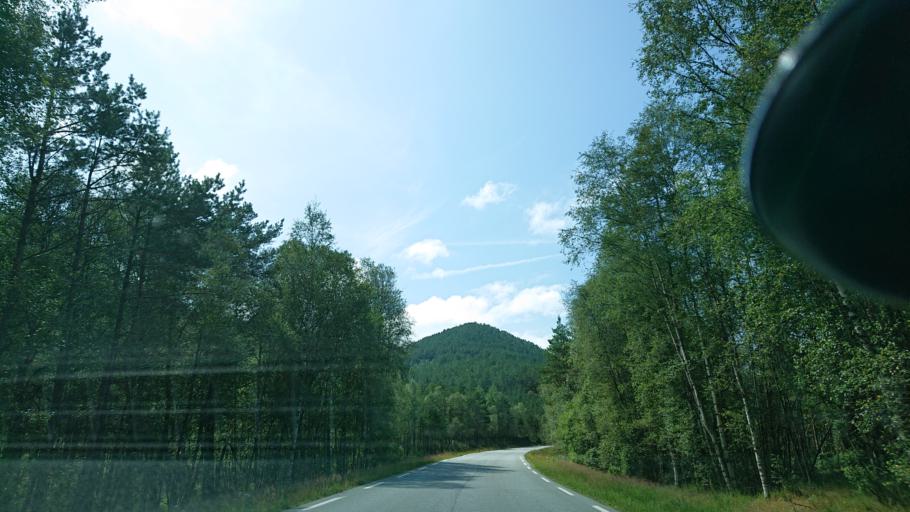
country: NO
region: Rogaland
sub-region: Hjelmeland
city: Hjelmelandsvagen
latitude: 59.2371
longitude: 6.2741
